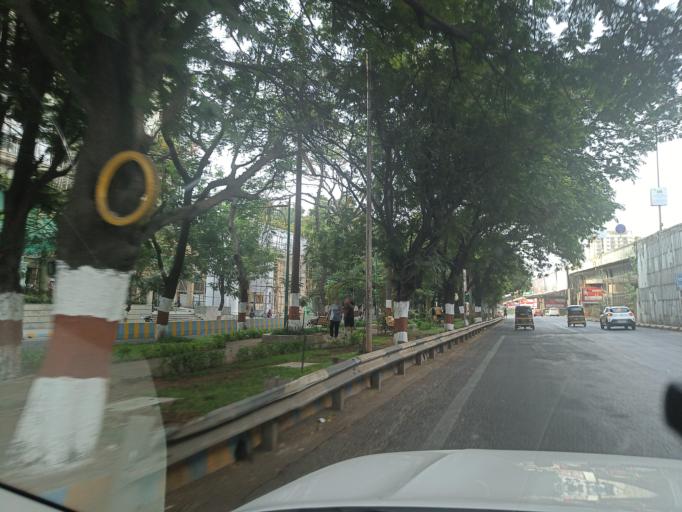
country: IN
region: Maharashtra
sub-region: Thane
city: Thane
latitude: 19.1898
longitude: 72.9636
